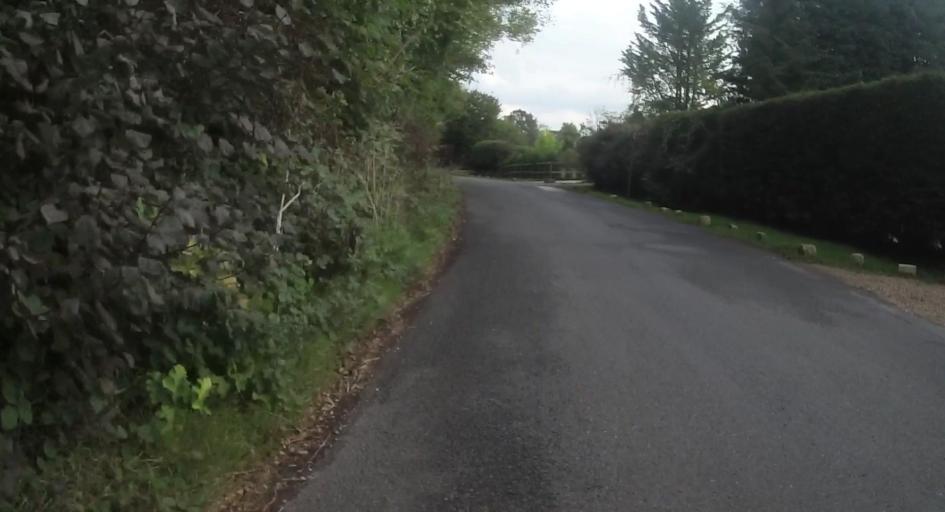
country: GB
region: England
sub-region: Hampshire
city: Tadley
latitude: 51.3997
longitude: -1.1813
